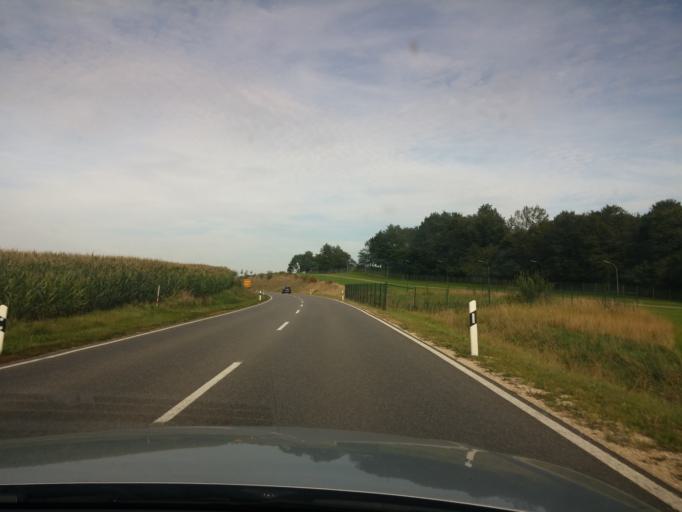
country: DE
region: Baden-Wuerttemberg
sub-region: Tuebingen Region
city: Biberach an der Riss
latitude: 48.1116
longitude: 9.7716
